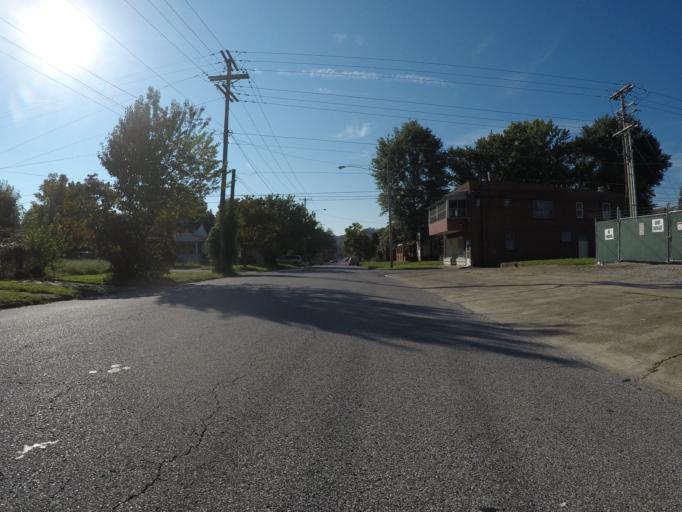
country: US
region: West Virginia
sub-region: Cabell County
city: Huntington
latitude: 38.4155
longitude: -82.4370
